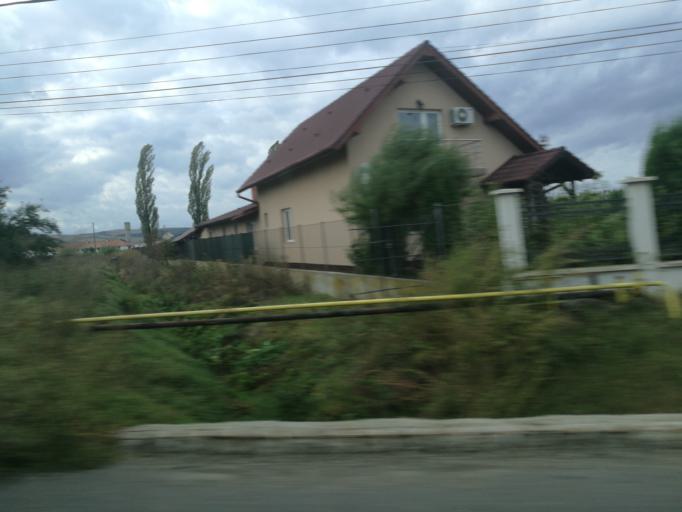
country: RO
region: Mures
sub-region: Comuna Cristesti
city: Cristesti
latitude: 46.4986
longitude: 24.4845
